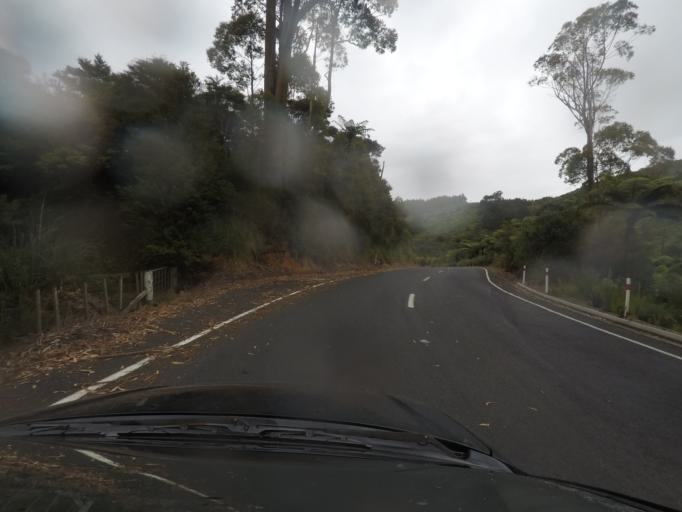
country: NZ
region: Auckland
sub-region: Auckland
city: Warkworth
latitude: -36.2782
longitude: 174.6908
